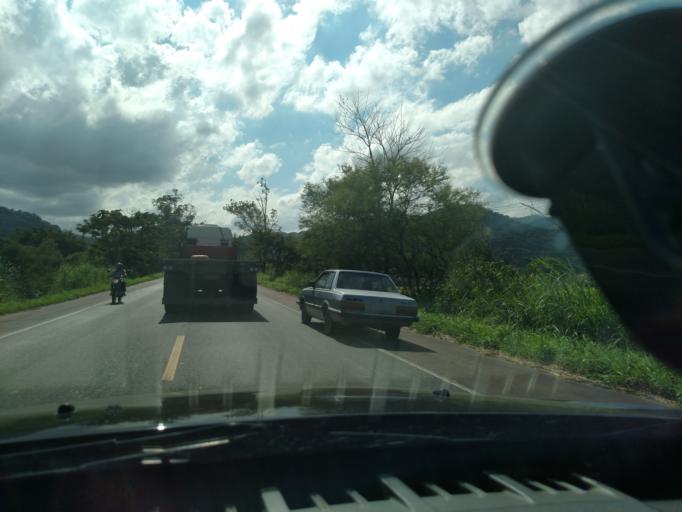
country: BR
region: Santa Catarina
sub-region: Rodeio
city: Gavea
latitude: -26.9498
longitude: -49.3125
